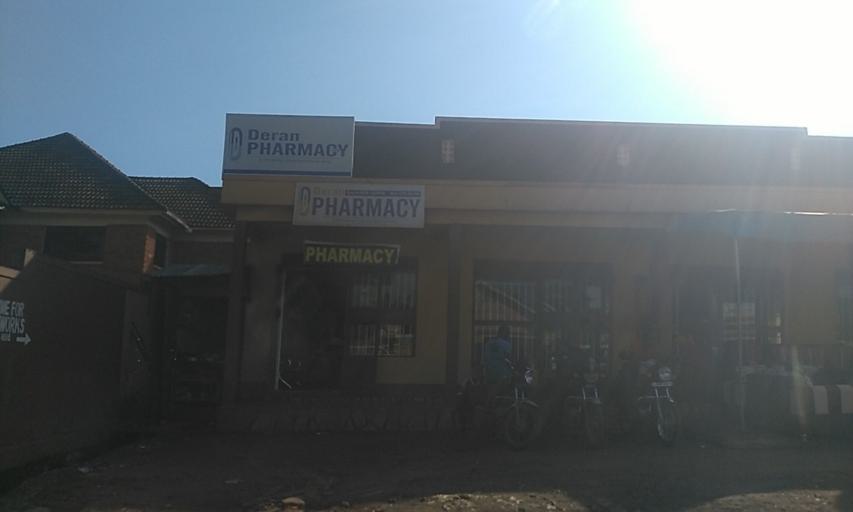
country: UG
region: Central Region
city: Kampala Central Division
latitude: 0.3214
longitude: 32.5448
